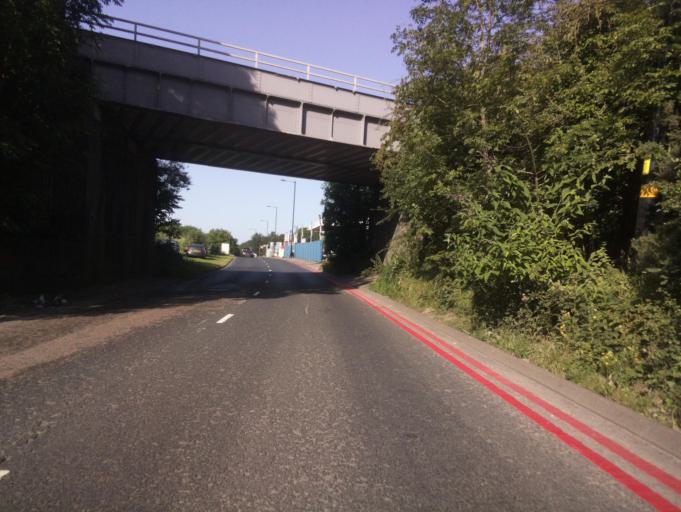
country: GB
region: England
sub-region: Warwickshire
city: Water Orton
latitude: 52.5278
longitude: -1.7832
